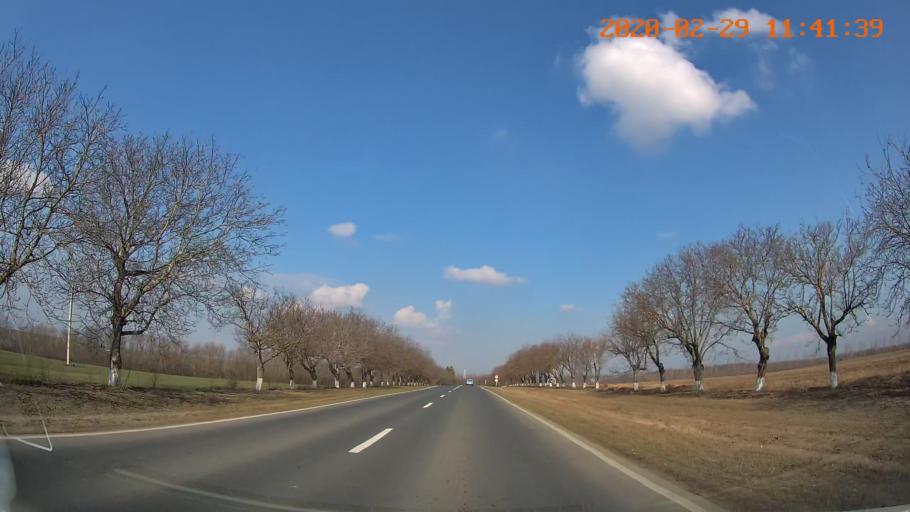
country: MD
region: Rezina
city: Saharna
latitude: 47.6745
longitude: 29.0157
